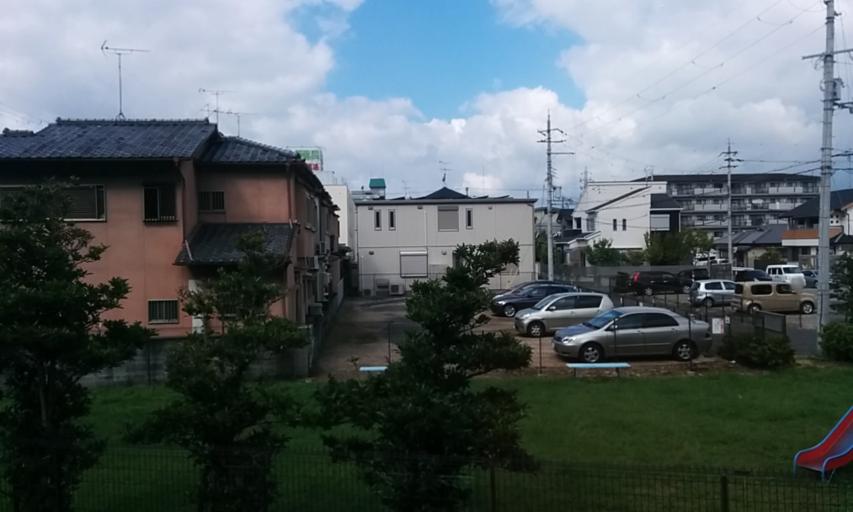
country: JP
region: Nara
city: Kashihara-shi
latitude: 34.5157
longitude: 135.7922
